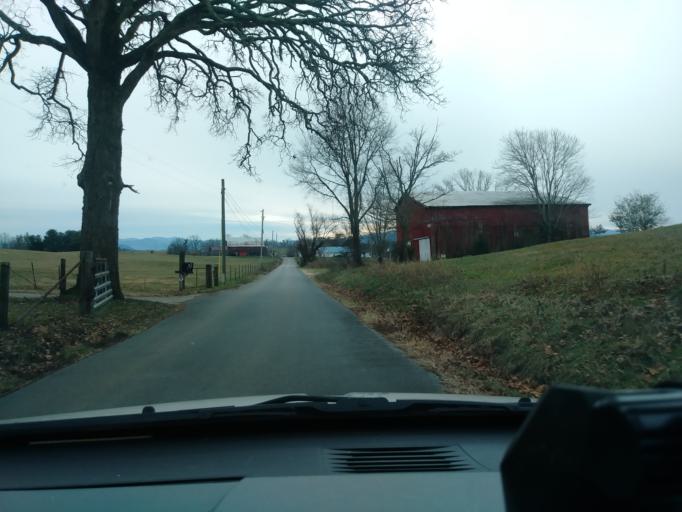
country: US
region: Tennessee
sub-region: Greene County
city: Greeneville
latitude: 36.0909
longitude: -82.8942
